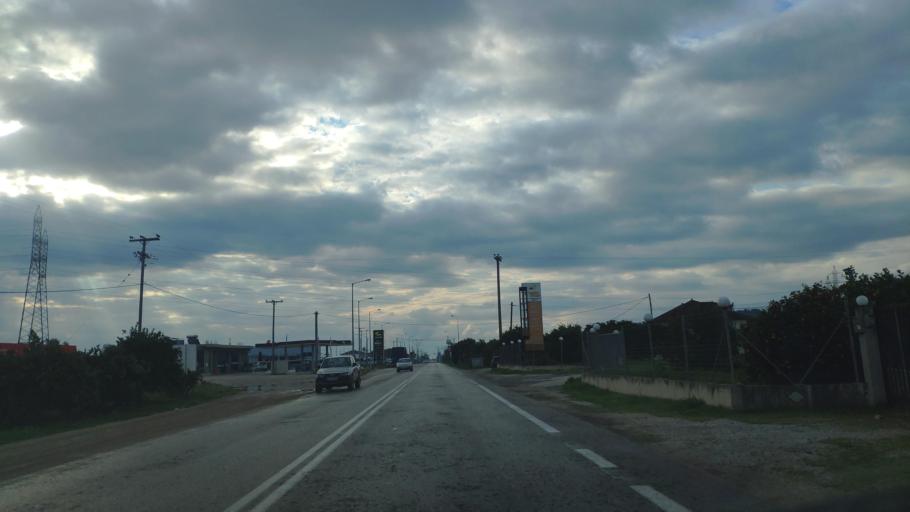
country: GR
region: Peloponnese
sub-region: Nomos Argolidos
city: Argos
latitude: 37.6584
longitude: 22.7262
